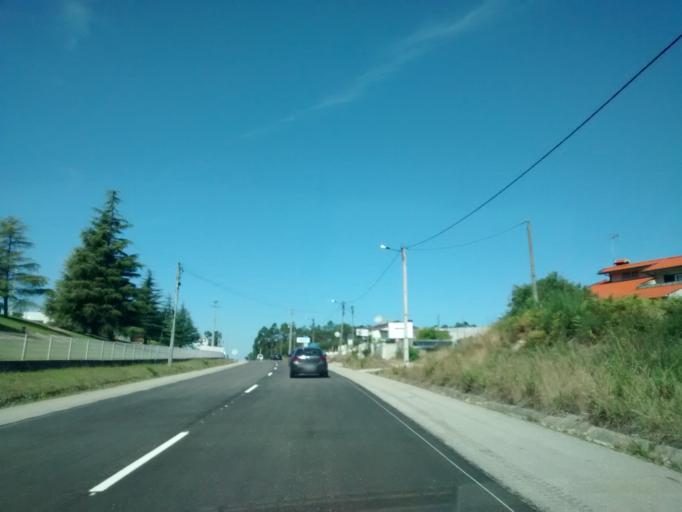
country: PT
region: Aveiro
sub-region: Oliveira do Bairro
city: Oia
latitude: 40.5371
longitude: -8.5184
